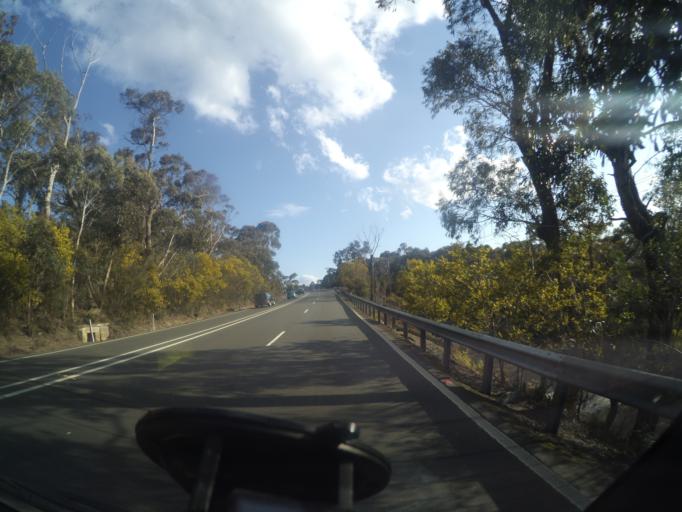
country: AU
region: New South Wales
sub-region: Blue Mountains Municipality
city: Katoomba
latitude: -33.6936
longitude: 150.2902
